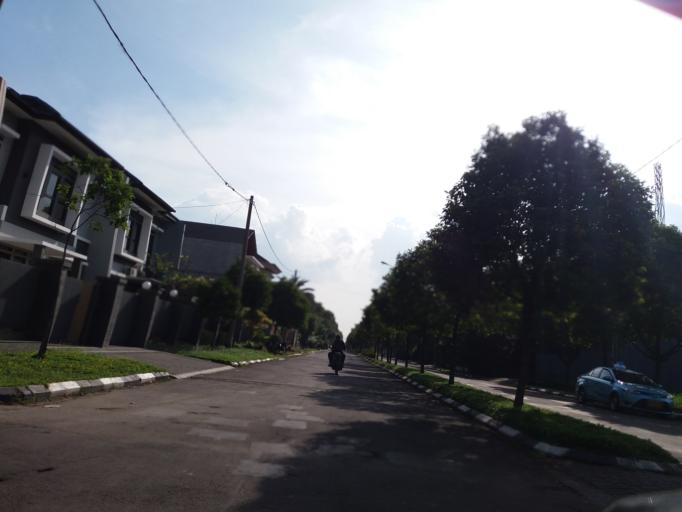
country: ID
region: West Java
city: Bandung
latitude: -6.9602
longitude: 107.6329
